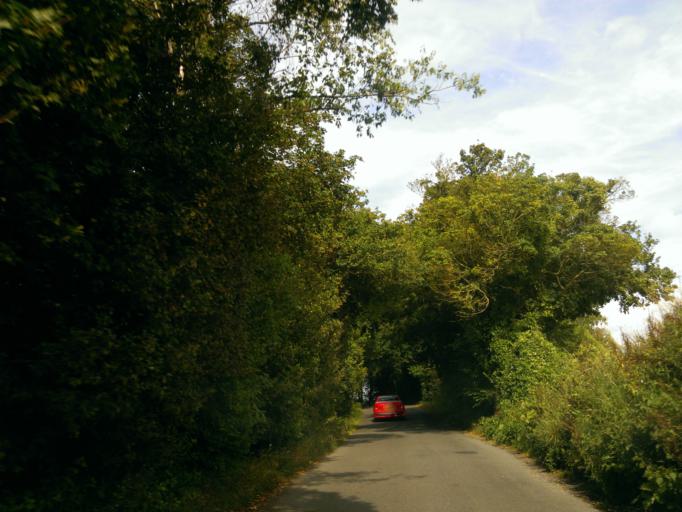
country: GB
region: England
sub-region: Essex
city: Sible Hedingham
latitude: 51.9785
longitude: 0.6147
